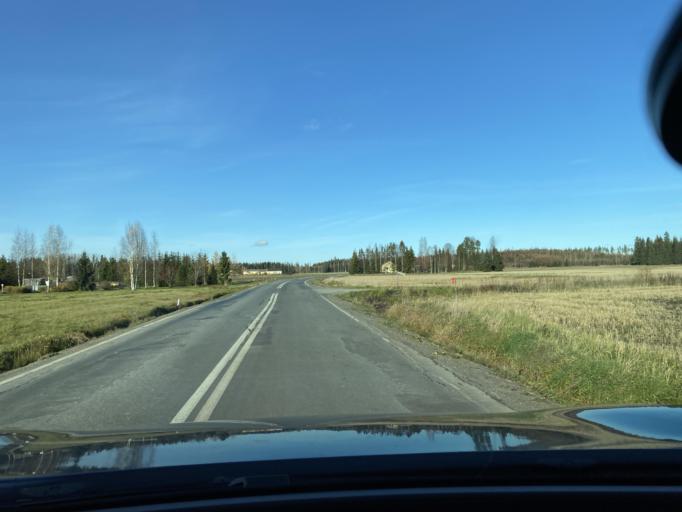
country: FI
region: Haeme
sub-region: Forssa
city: Tammela
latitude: 60.8311
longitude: 23.8402
